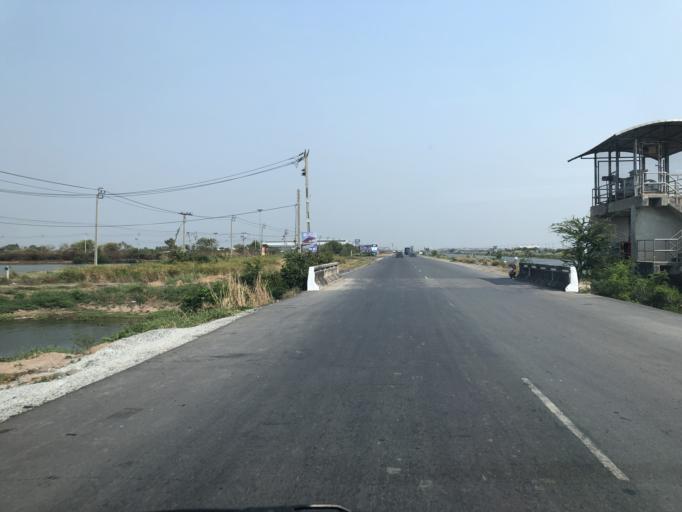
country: TH
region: Samut Prakan
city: Bang Bo District
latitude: 13.5341
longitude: 100.7493
